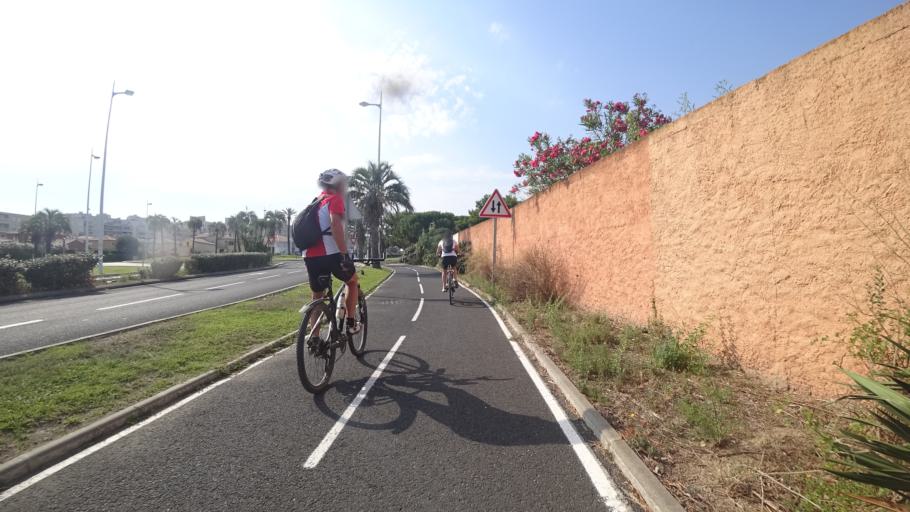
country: FR
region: Languedoc-Roussillon
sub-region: Departement des Pyrenees-Orientales
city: Canet-en-Roussillon
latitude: 42.6771
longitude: 3.0302
